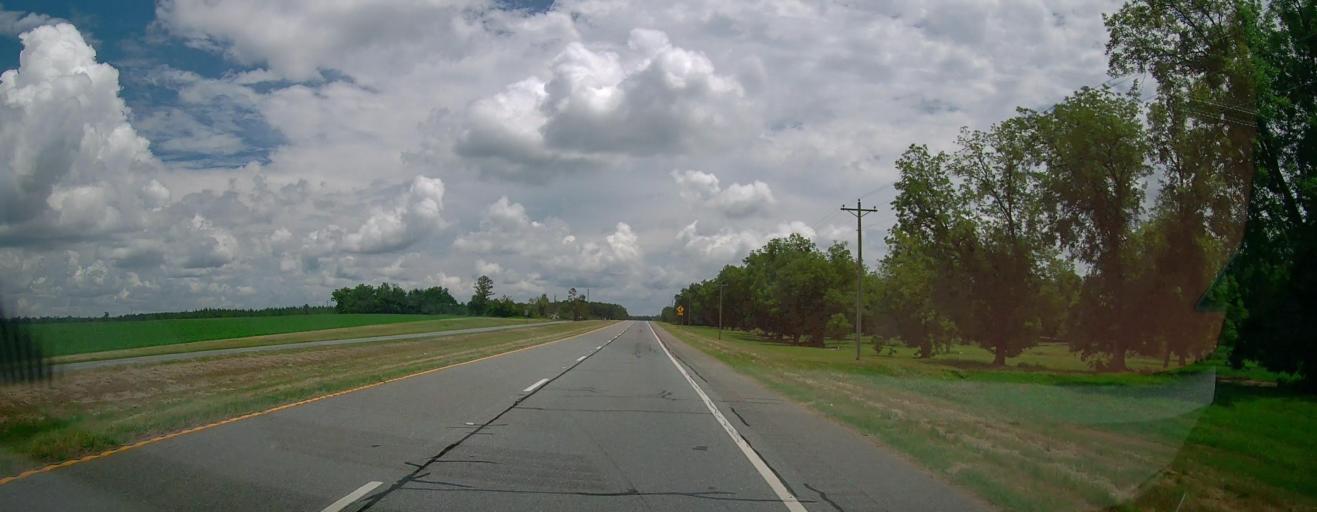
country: US
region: Georgia
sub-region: Pulaski County
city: Hawkinsville
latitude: 32.2584
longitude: -83.3983
